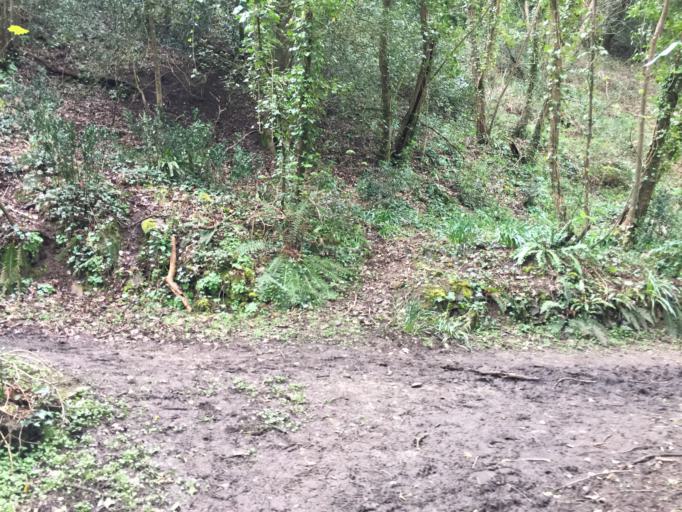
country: JE
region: St Helier
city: Saint Helier
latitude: 49.2120
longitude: -2.1329
